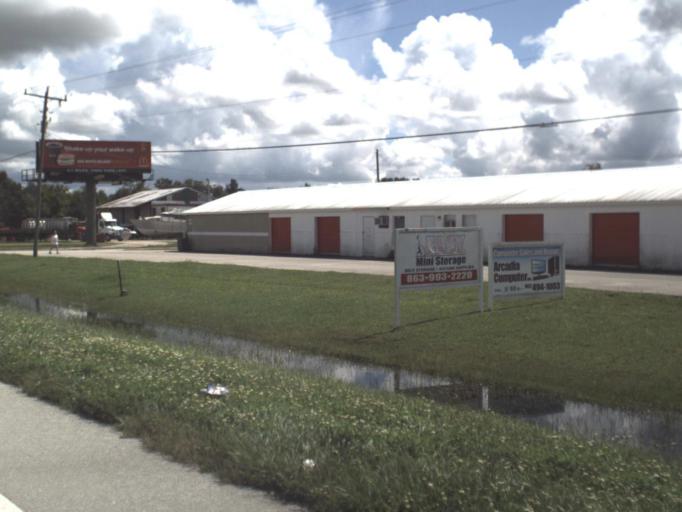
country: US
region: Florida
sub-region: DeSoto County
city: Arcadia
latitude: 27.2311
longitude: -81.9182
